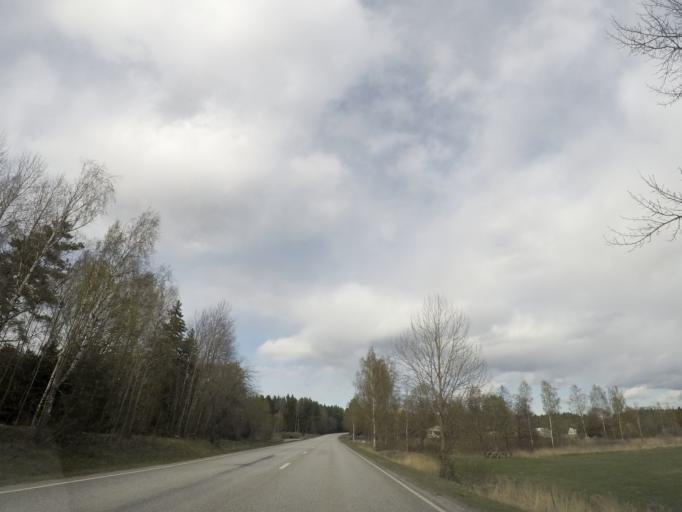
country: SE
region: Vaestmanland
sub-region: Kungsors Kommun
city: Kungsoer
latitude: 59.2984
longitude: 16.2131
